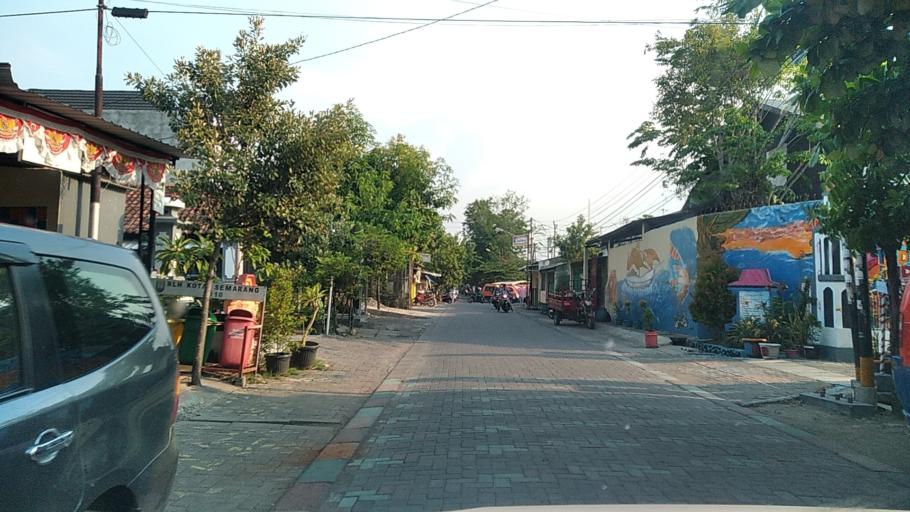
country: ID
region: Central Java
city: Semarang
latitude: -6.9659
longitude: 110.4061
